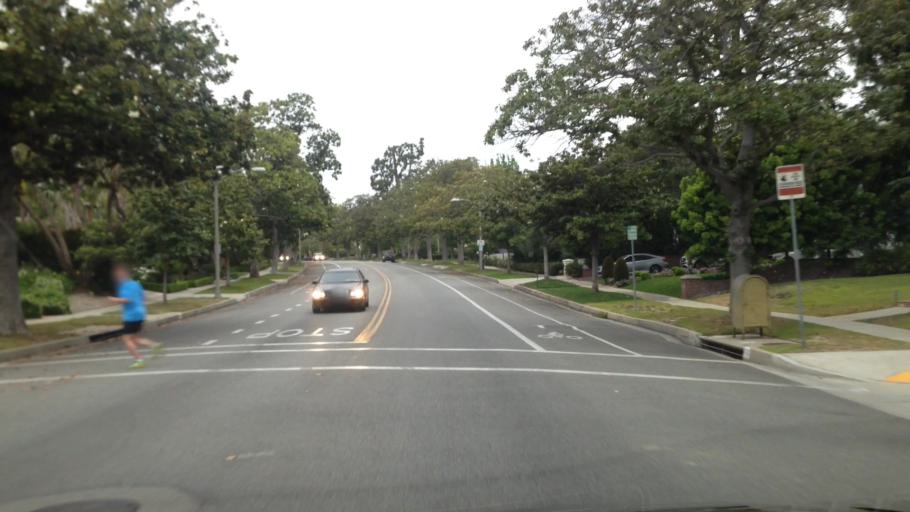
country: US
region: California
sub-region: Los Angeles County
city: Beverly Hills
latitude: 34.0791
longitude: -118.4066
